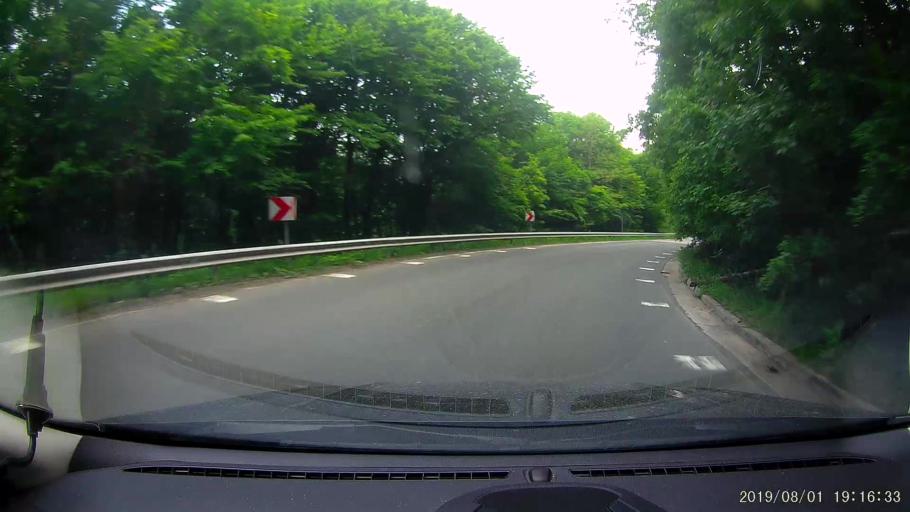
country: BG
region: Shumen
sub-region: Obshtina Smyadovo
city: Smyadovo
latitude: 42.9327
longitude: 26.9514
